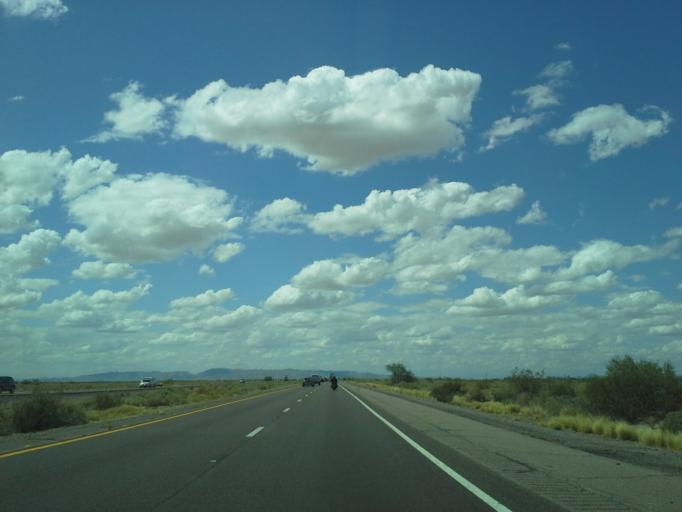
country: US
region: Arizona
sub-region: Pinal County
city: Casa Blanca
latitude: 33.1543
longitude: -111.8698
